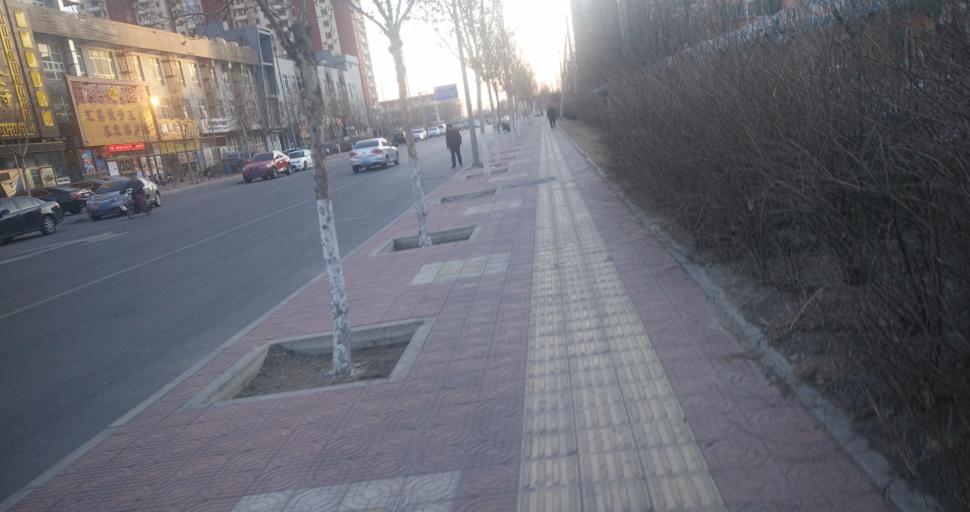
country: CN
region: Beijing
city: Yinghai
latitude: 39.7584
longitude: 116.4961
